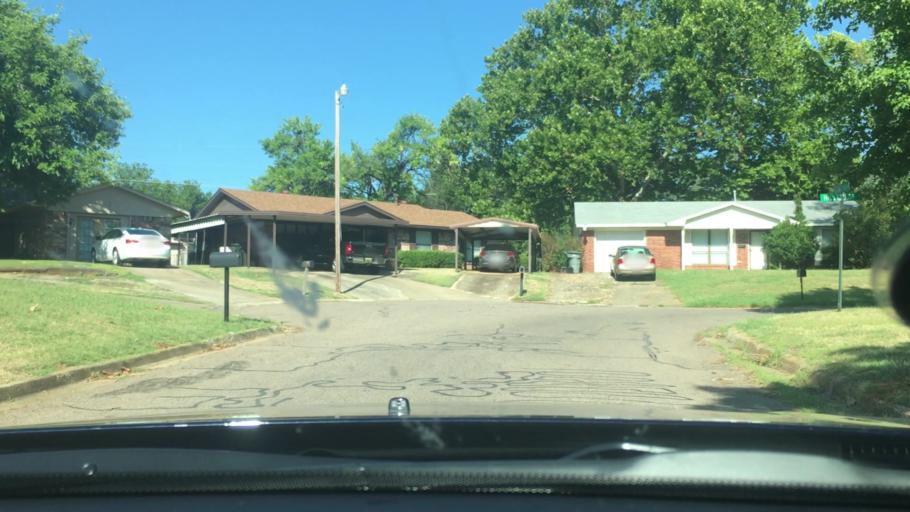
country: US
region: Oklahoma
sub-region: Bryan County
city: Durant
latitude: 34.0126
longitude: -96.3875
